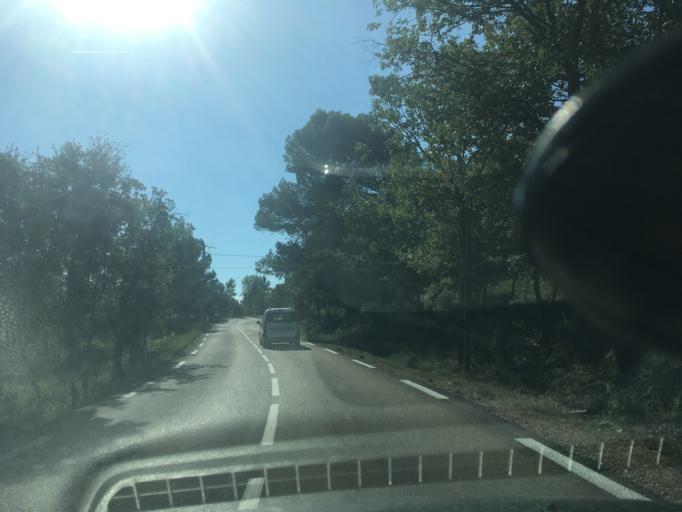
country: FR
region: Provence-Alpes-Cote d'Azur
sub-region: Departement du Var
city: Barjols
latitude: 43.6056
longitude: 6.0684
